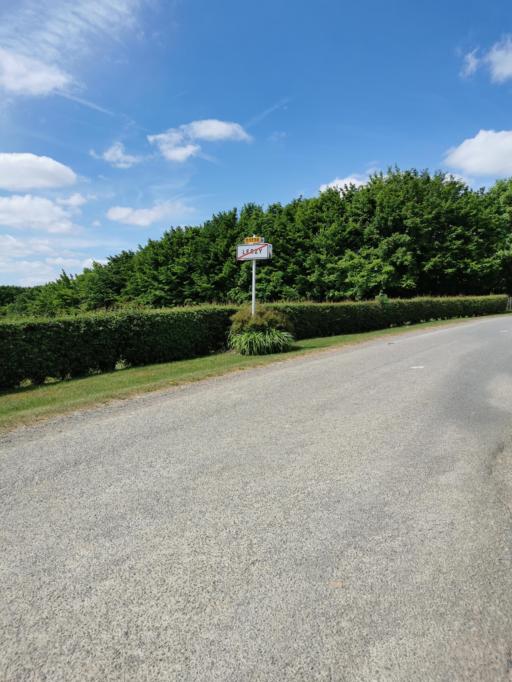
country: FR
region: Picardie
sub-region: Departement de l'Aisne
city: Buironfosse
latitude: 49.9465
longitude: 3.8738
